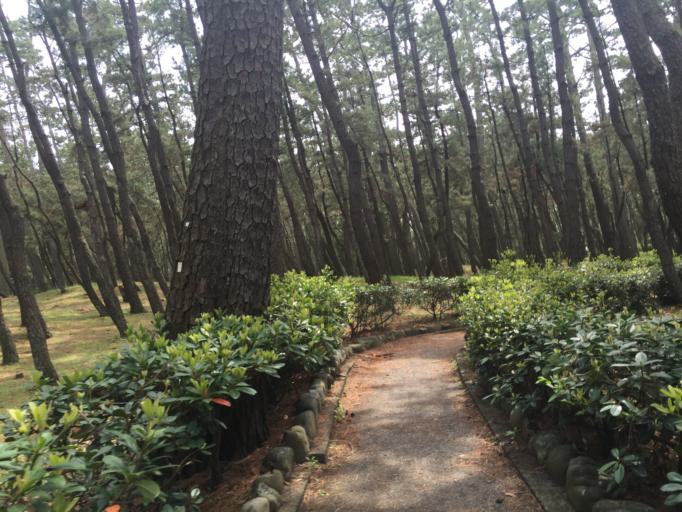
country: JP
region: Shizuoka
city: Numazu
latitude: 35.0929
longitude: 138.8487
